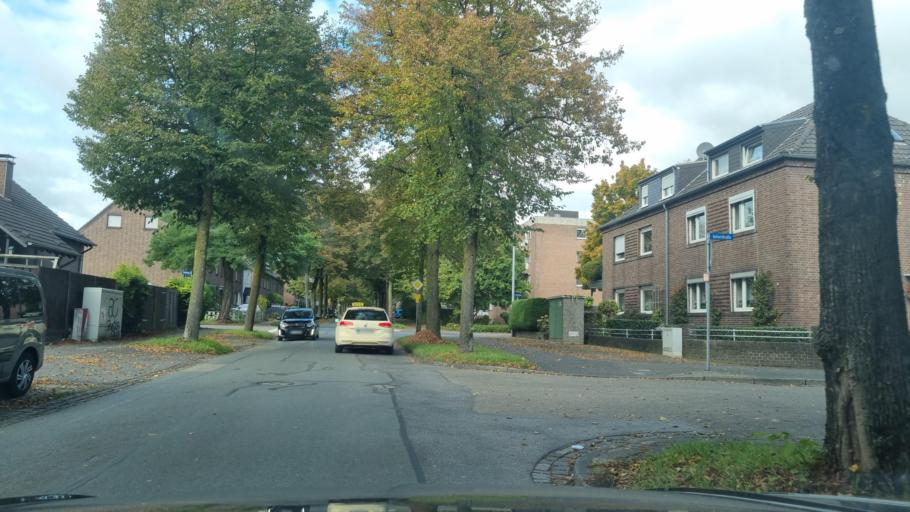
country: DE
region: North Rhine-Westphalia
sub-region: Regierungsbezirk Dusseldorf
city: Kleve
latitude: 51.7778
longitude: 6.1173
